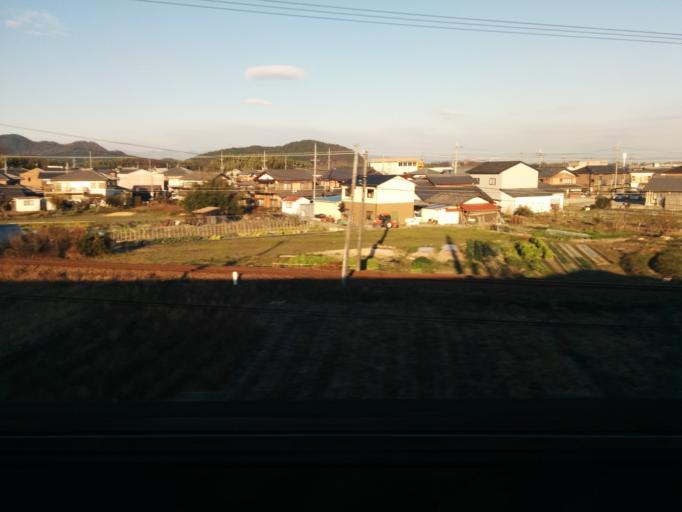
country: JP
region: Shiga Prefecture
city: Youkaichi
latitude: 35.1674
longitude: 136.2073
